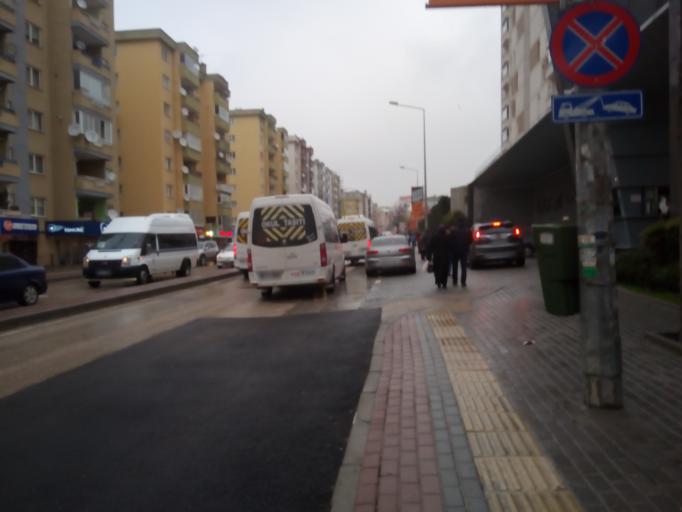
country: TR
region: Bursa
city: Niluefer
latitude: 40.2528
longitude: 28.9574
